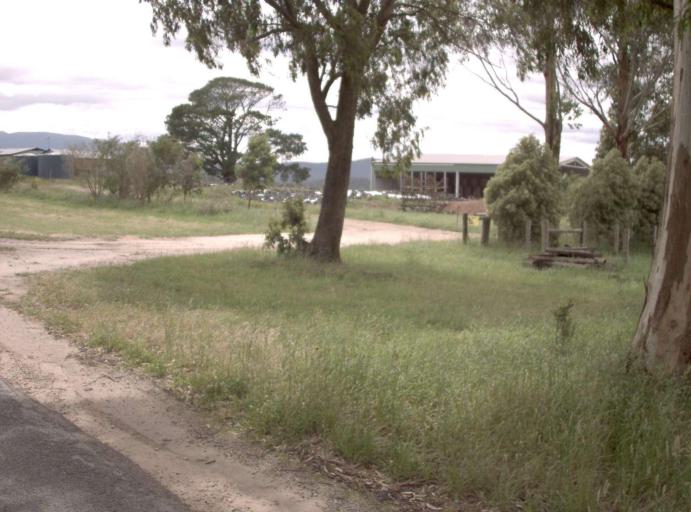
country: AU
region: Victoria
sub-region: Latrobe
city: Moe
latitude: -37.9981
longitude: 146.1458
